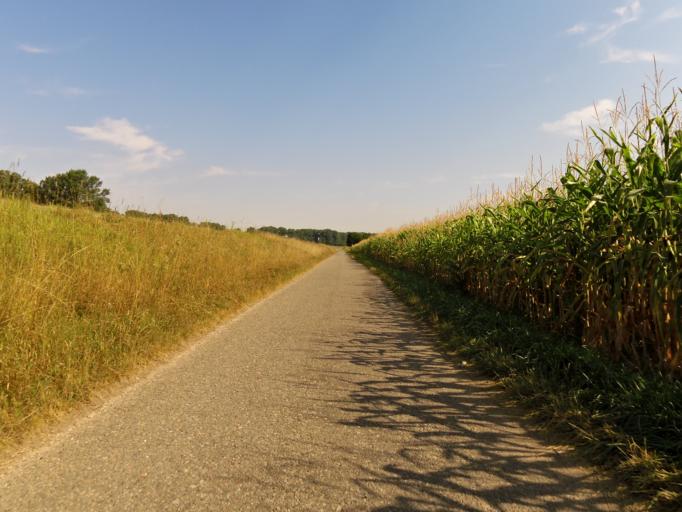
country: DE
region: Hesse
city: Lampertheim
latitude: 49.5547
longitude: 8.4215
